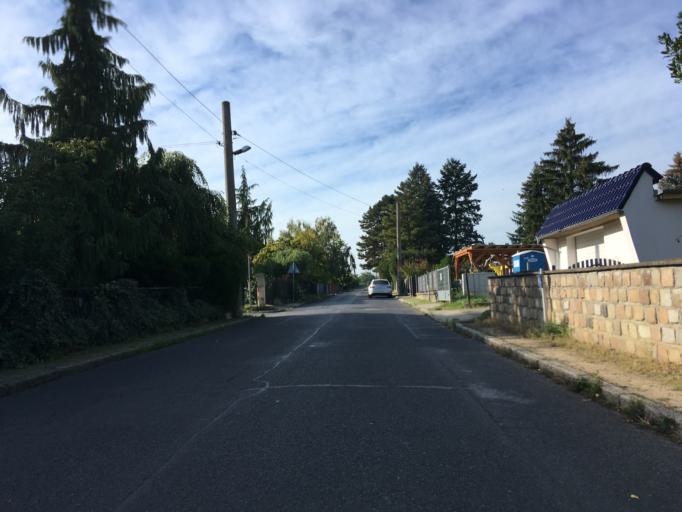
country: DE
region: Brandenburg
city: Hoppegarten
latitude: 52.5191
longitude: 13.6560
